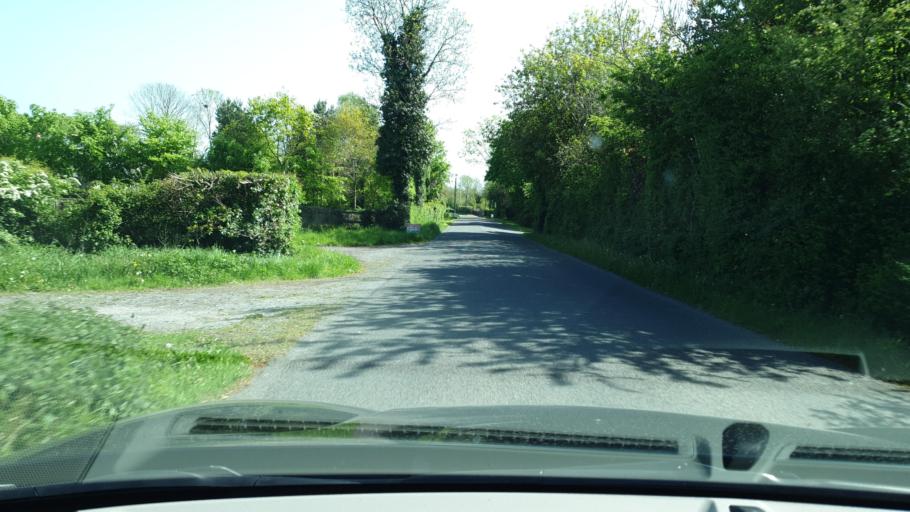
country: IE
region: Leinster
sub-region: Kildare
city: Maynooth
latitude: 53.4280
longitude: -6.5760
